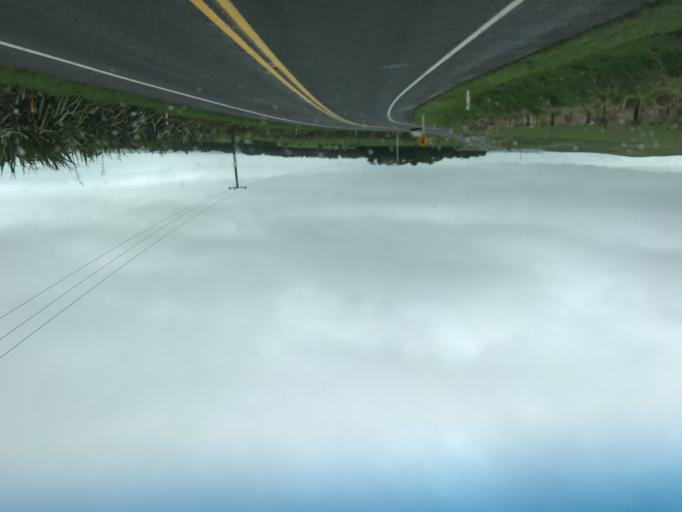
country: NZ
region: Manawatu-Wanganui
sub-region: Wanganui District
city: Wanganui
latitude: -39.8133
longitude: 174.7937
